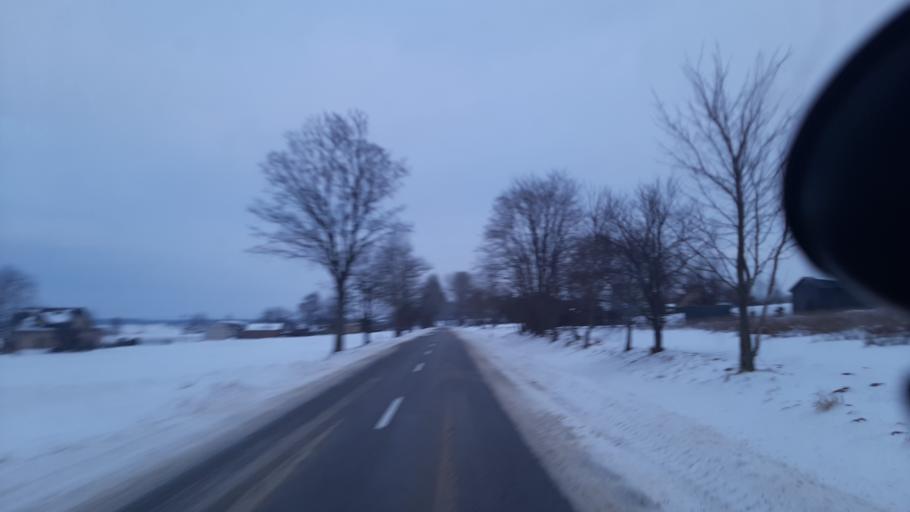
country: PL
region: Lublin Voivodeship
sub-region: Powiat lubelski
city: Garbow
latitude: 51.3460
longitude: 22.3847
